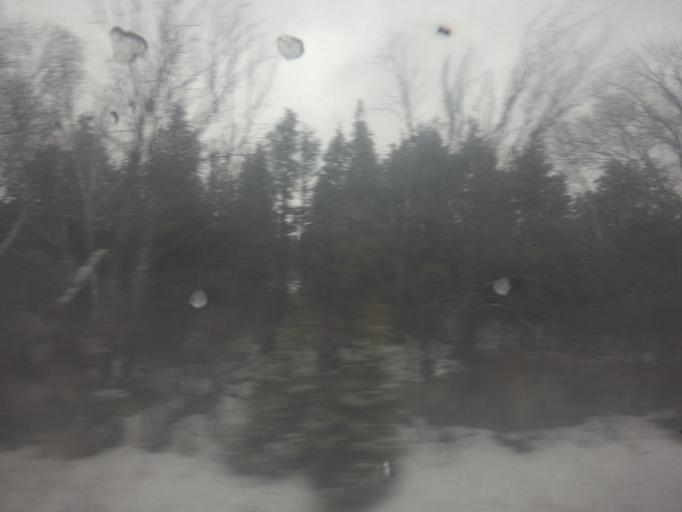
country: CA
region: Ontario
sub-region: Lanark County
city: Smiths Falls
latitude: 44.9526
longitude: -76.0101
